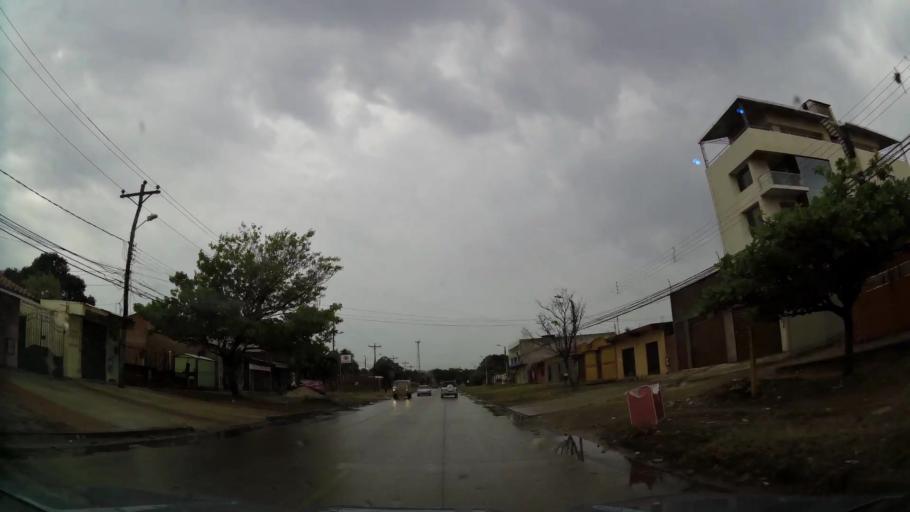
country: BO
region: Santa Cruz
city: Santa Cruz de la Sierra
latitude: -17.7810
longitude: -63.1430
